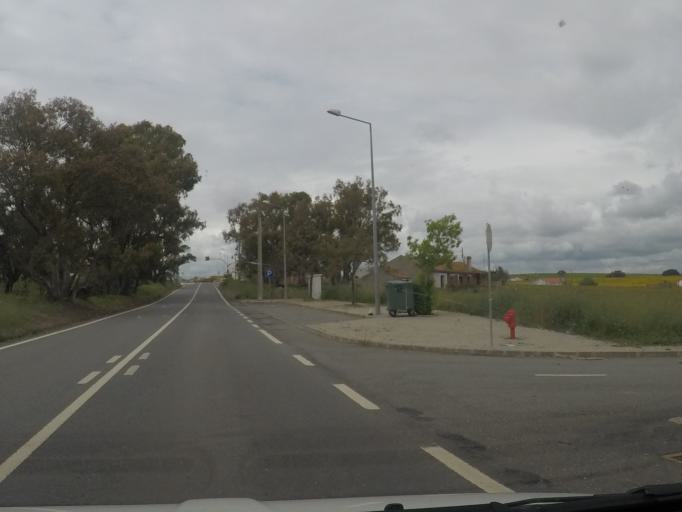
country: PT
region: Setubal
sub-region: Sines
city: Porto Covo
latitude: 37.8638
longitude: -8.7187
